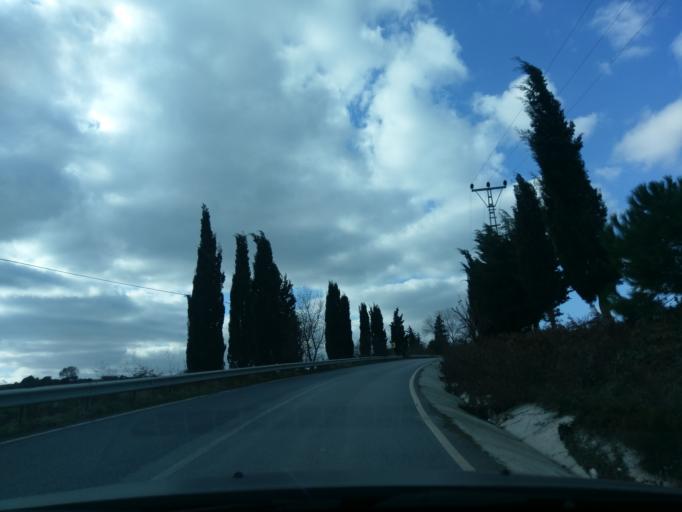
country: TR
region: Istanbul
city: Durusu
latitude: 41.3099
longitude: 28.6936
